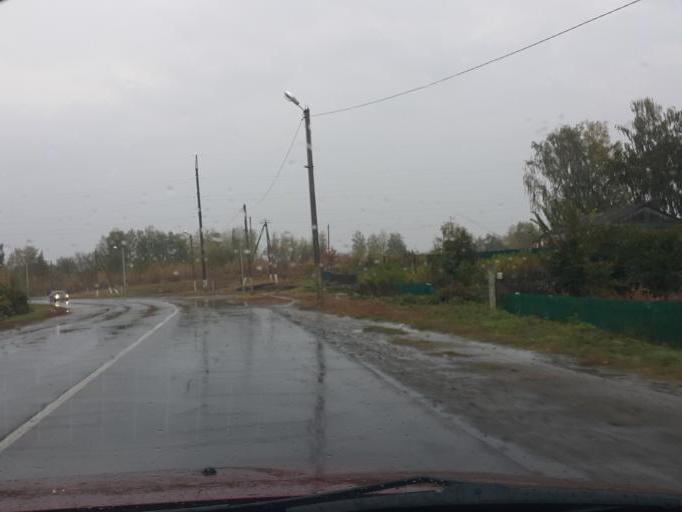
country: RU
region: Tambov
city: Znamenka
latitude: 52.4065
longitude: 41.4598
